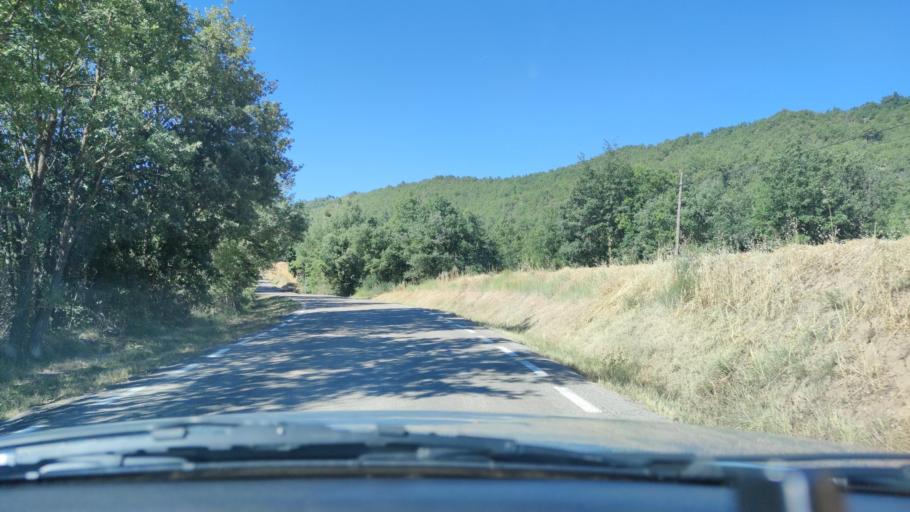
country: ES
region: Catalonia
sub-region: Provincia de Lleida
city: Solsona
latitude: 41.9648
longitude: 1.4957
